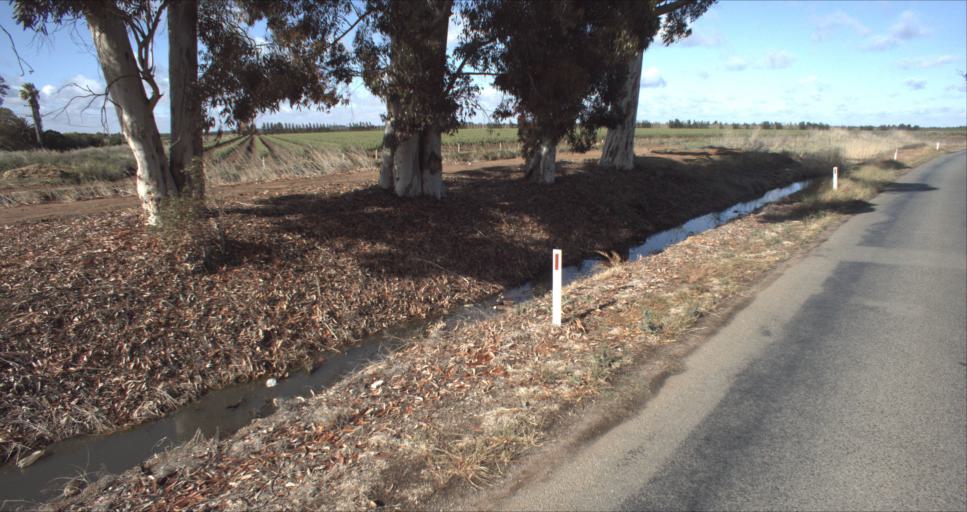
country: AU
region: New South Wales
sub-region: Leeton
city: Leeton
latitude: -34.5528
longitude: 146.3777
